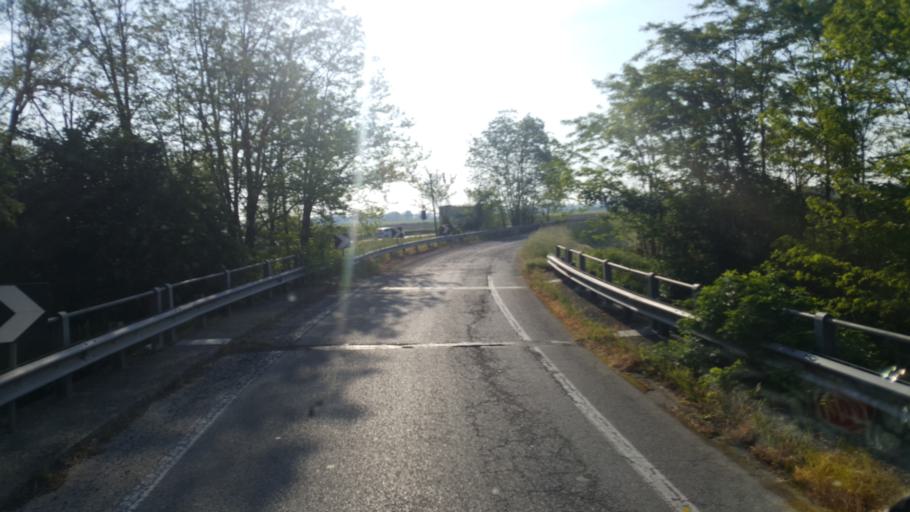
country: IT
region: Lombardy
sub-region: Provincia di Cremona
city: Santa Maria dei Sabbioni
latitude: 45.2412
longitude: 9.8438
